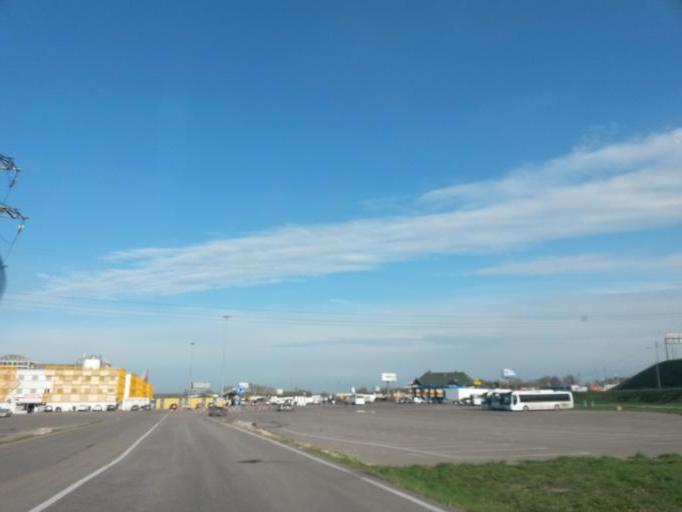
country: RU
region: Moscow
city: Zyablikovo
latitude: 55.6200
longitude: 37.7789
